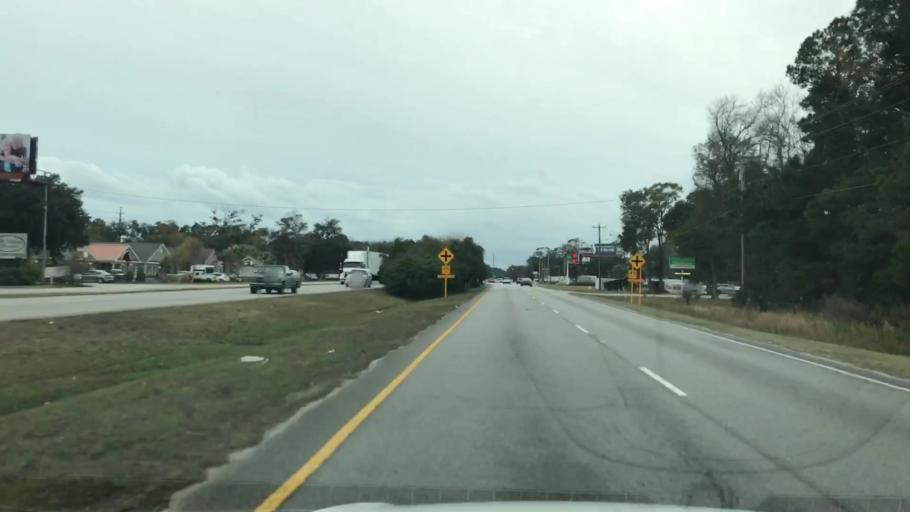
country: US
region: South Carolina
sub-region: Georgetown County
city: Murrells Inlet
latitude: 33.5384
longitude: -79.0562
